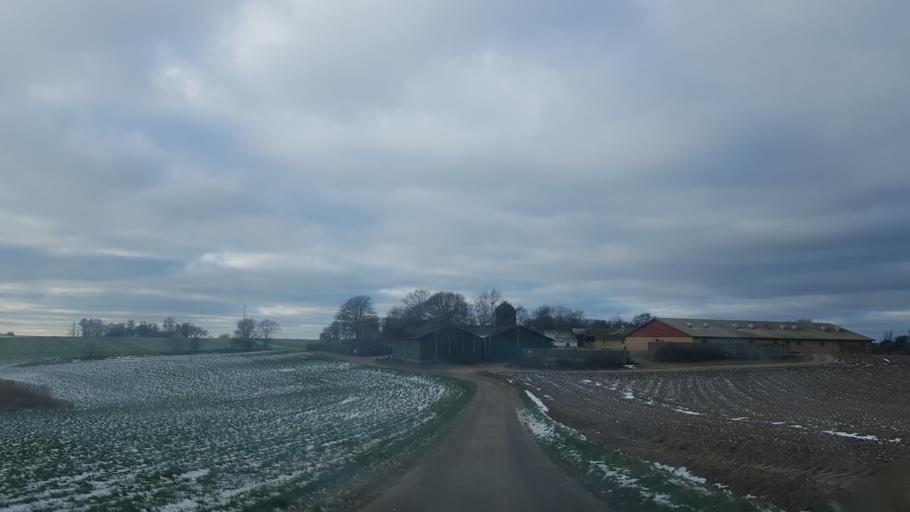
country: DK
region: Zealand
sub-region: Odsherred Kommune
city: Hojby
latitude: 55.9240
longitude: 11.5727
